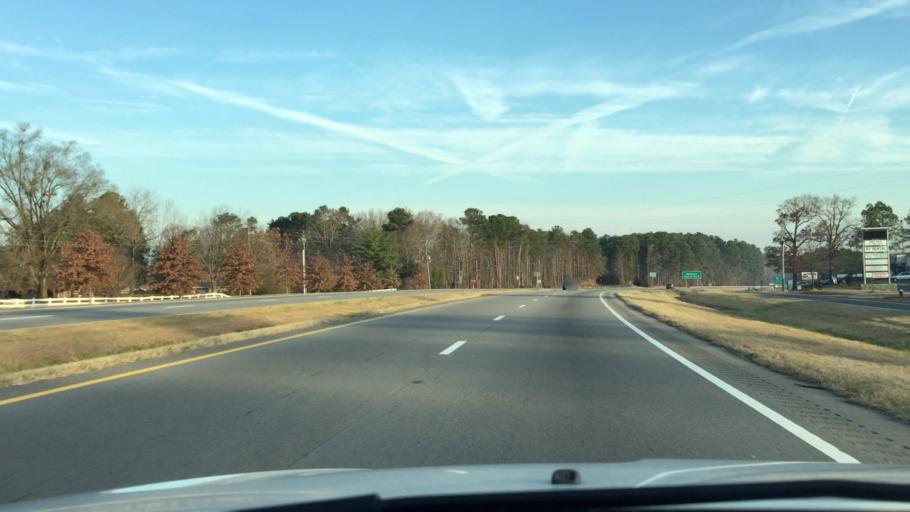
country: US
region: North Carolina
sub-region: Lee County
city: Sanford
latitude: 35.4490
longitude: -79.2148
